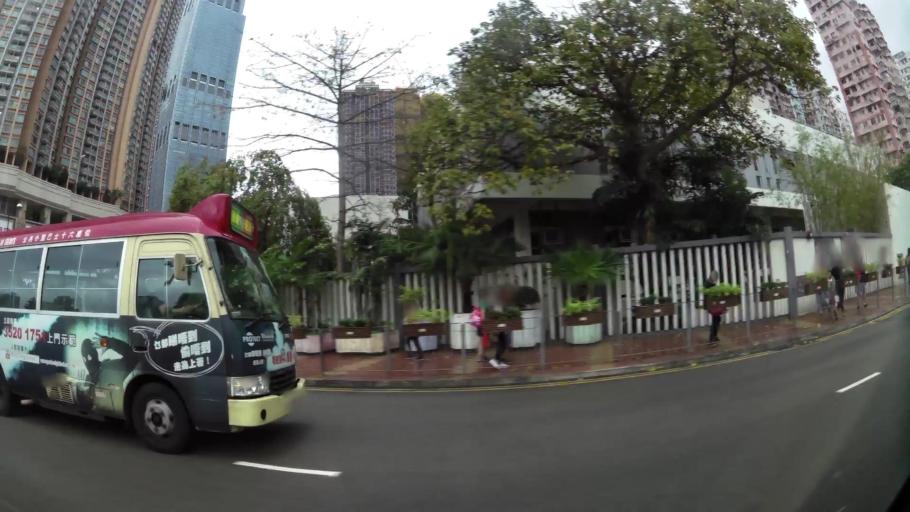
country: HK
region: Tsuen Wan
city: Tsuen Wan
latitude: 22.3714
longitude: 114.1133
